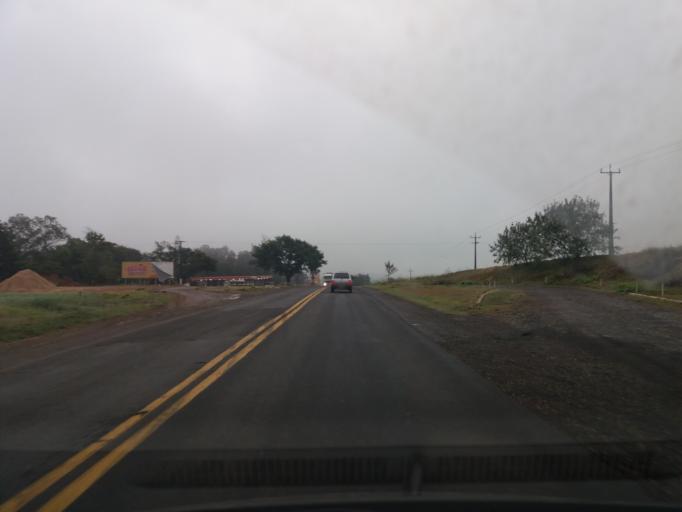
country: BR
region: Parana
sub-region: Realeza
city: Realeza
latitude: -25.8166
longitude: -53.5194
